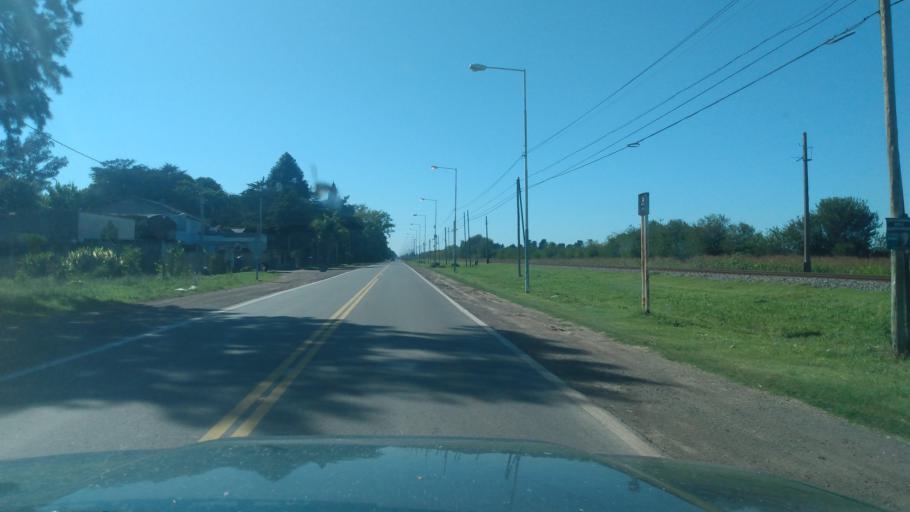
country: AR
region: Buenos Aires
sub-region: Partido de General Rodriguez
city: General Rodriguez
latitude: -34.5923
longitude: -59.0232
